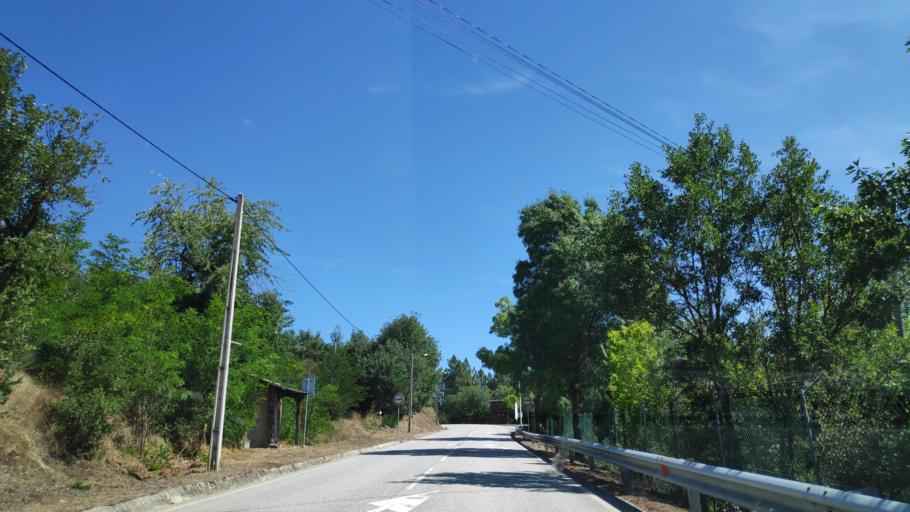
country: PT
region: Braganca
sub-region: Braganca Municipality
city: Braganca
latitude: 41.8431
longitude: -6.7478
